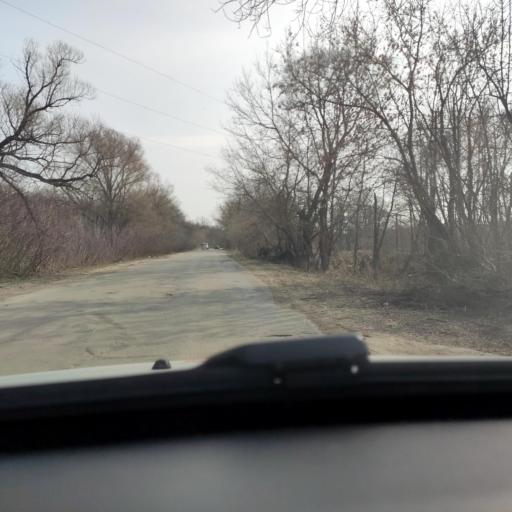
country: RU
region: Voronezj
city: Ramon'
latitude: 51.9077
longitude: 39.3587
